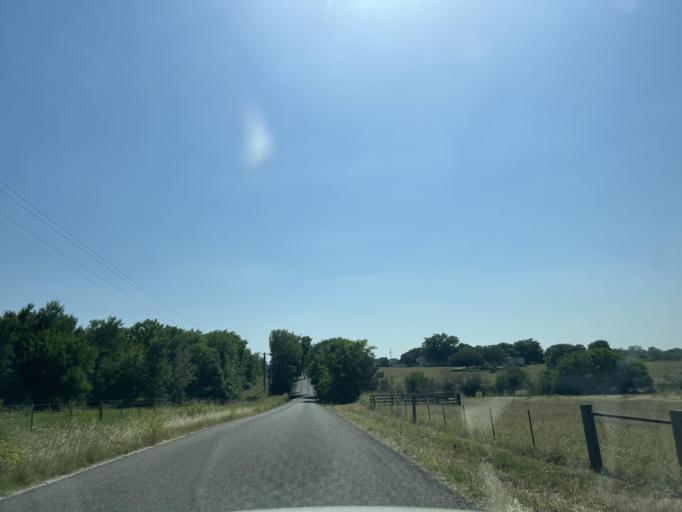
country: US
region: Texas
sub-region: Washington County
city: Brenham
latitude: 30.1576
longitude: -96.3470
